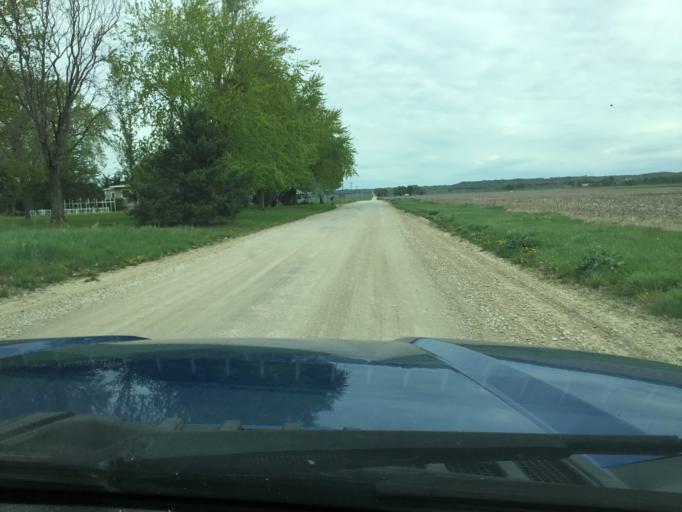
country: US
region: Kansas
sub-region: Douglas County
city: Lawrence
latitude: 39.0093
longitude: -95.2241
